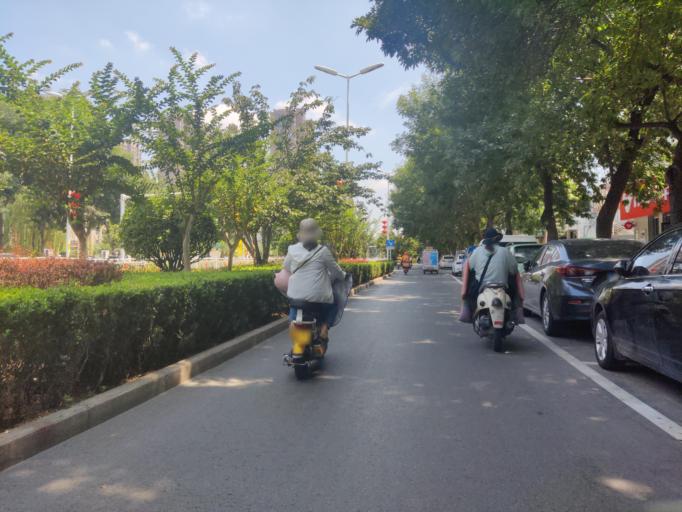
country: CN
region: Henan Sheng
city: Puyang
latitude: 35.7721
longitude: 115.0299
